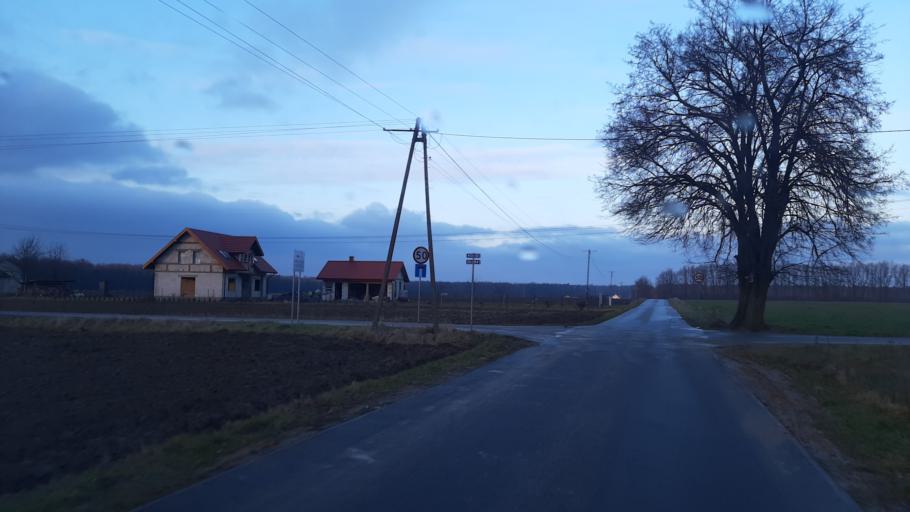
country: PL
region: Lublin Voivodeship
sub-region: Powiat lubelski
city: Garbow
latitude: 51.3646
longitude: 22.3976
